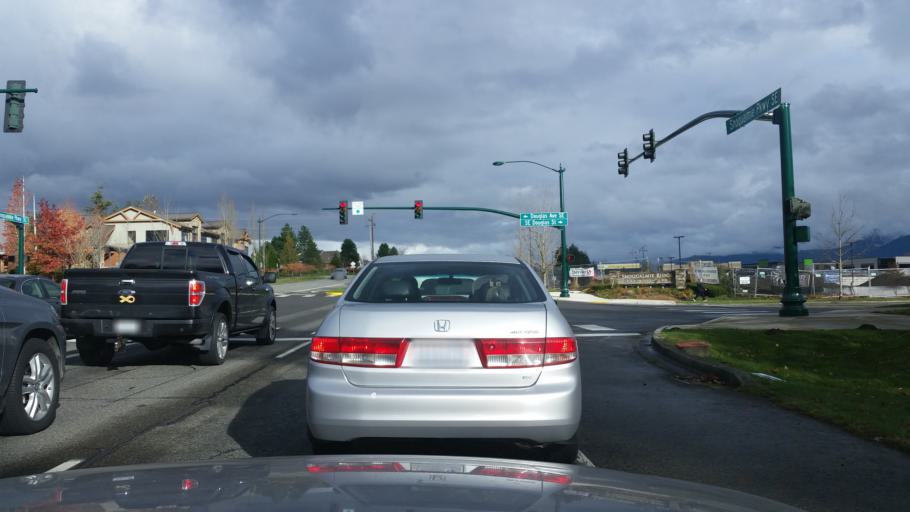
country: US
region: Washington
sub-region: King County
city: Fall City
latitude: 47.5277
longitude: -121.8765
